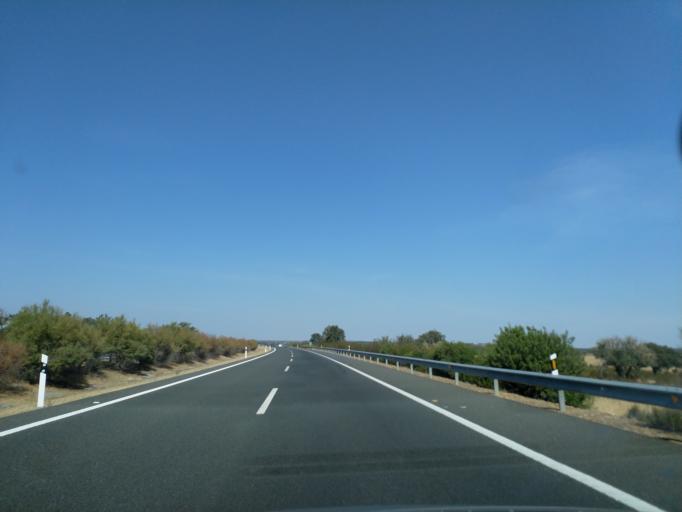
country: ES
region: Extremadura
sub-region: Provincia de Caceres
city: Casas de Don Antonio
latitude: 39.2109
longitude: -6.2861
